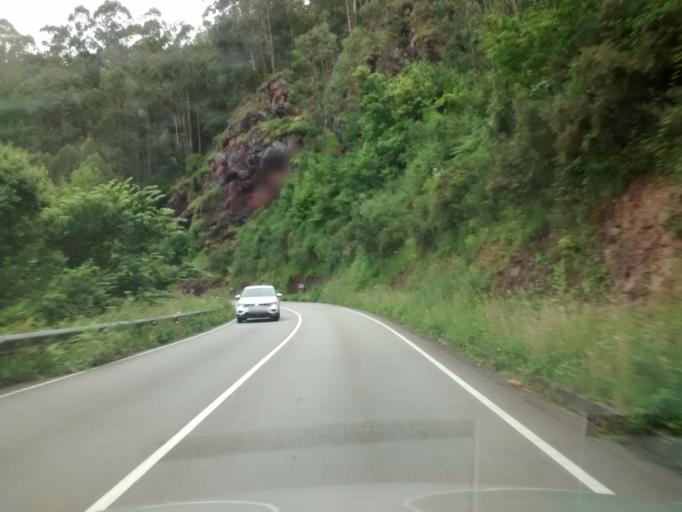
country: ES
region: Asturias
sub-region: Province of Asturias
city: Villaviciosa
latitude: 43.4473
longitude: -5.4386
